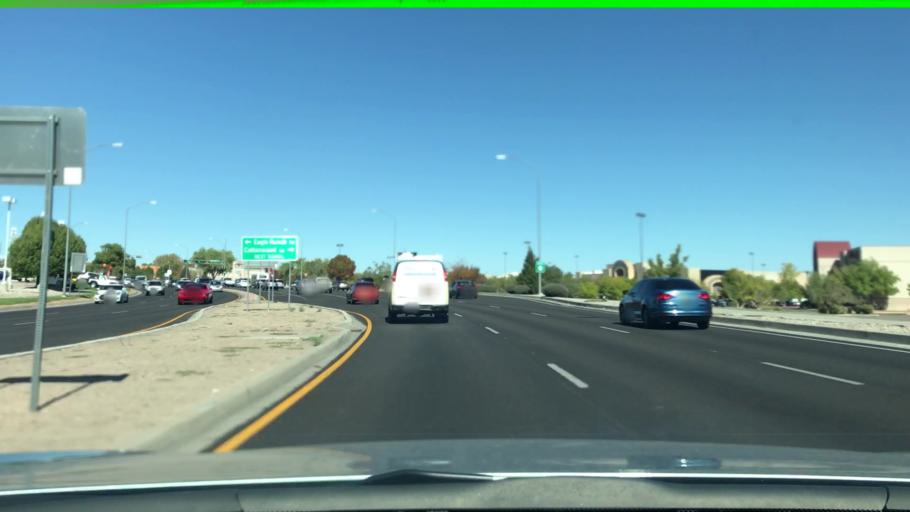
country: US
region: New Mexico
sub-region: Bernalillo County
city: Los Ranchos de Albuquerque
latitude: 35.1942
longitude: -106.6569
